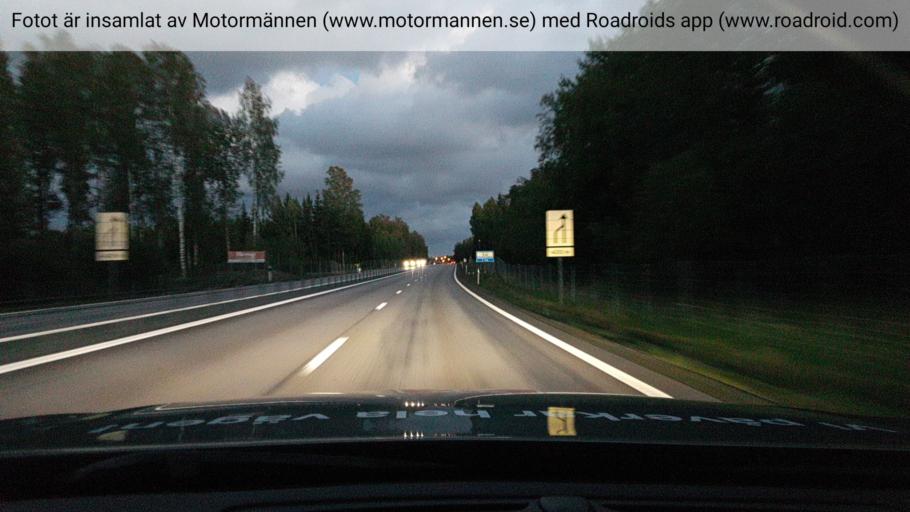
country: SE
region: Vaermland
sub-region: Kristinehamns Kommun
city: Kristinehamn
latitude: 59.3676
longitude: 14.0183
